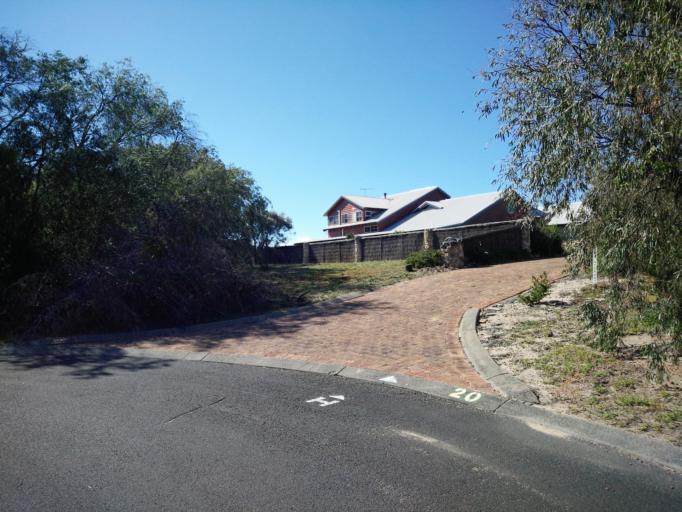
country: AU
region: Western Australia
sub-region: Capel
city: Capel
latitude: -33.5309
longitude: 115.5035
